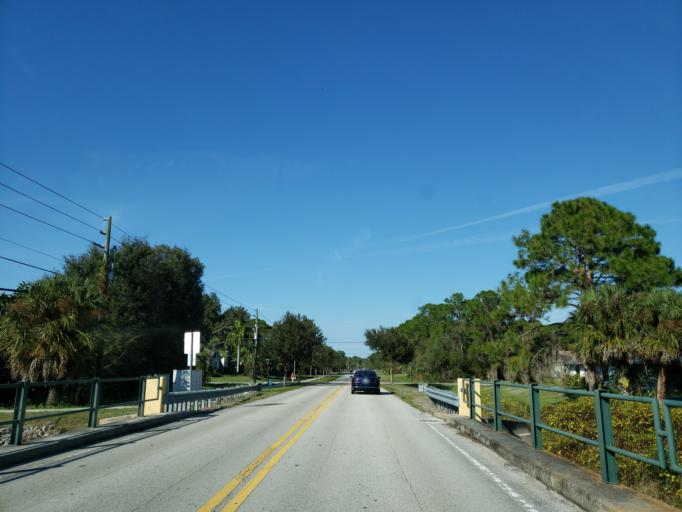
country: US
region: Florida
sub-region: Sarasota County
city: North Port
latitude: 27.0765
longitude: -82.1952
